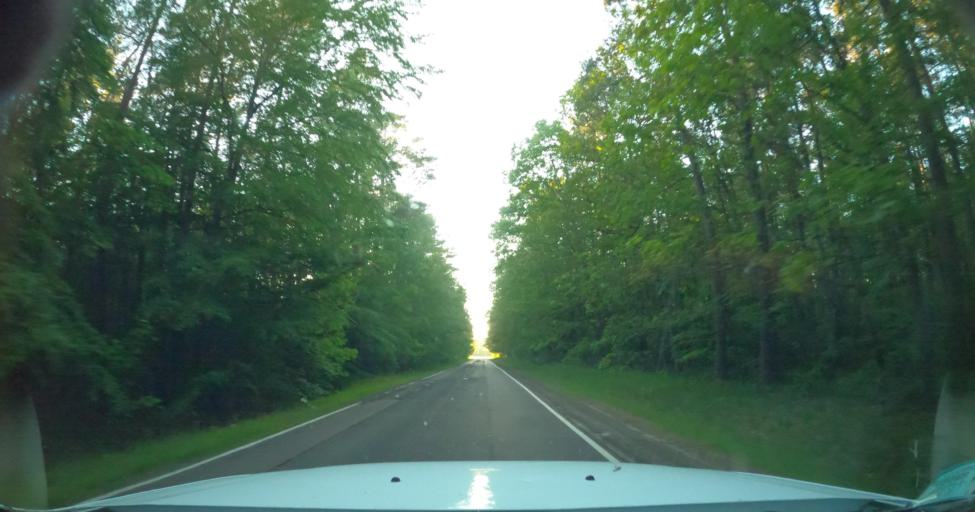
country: PL
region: Pomeranian Voivodeship
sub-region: Powiat bytowski
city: Czarna Dabrowka
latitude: 54.3828
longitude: 17.4855
